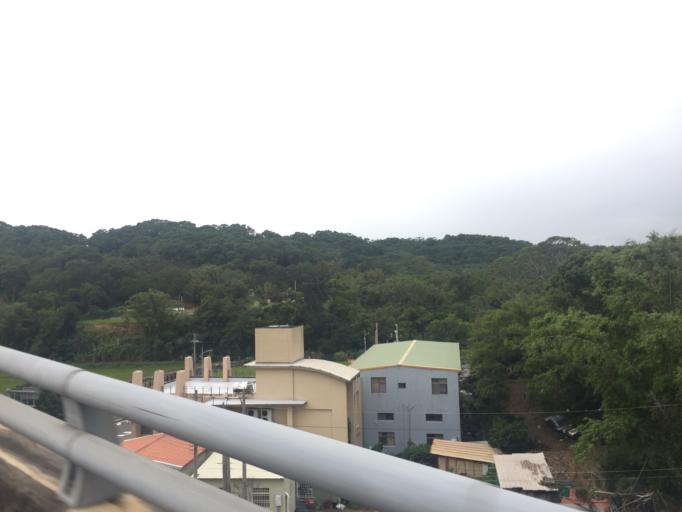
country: TW
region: Taiwan
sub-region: Hsinchu
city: Hsinchu
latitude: 24.7732
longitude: 120.9528
